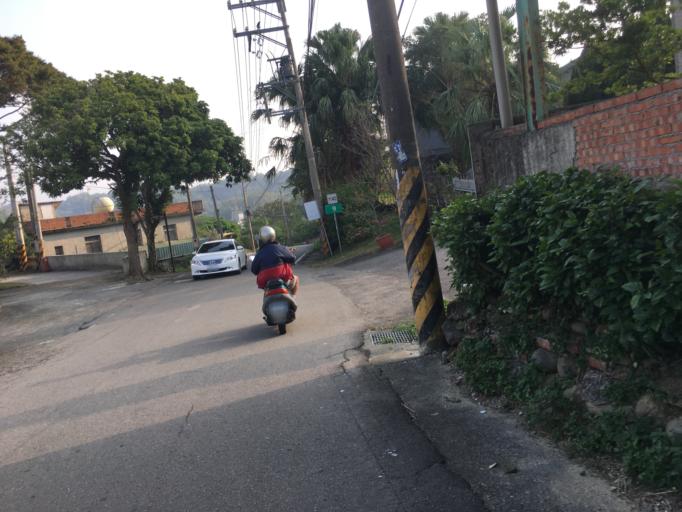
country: TW
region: Taiwan
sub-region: Hsinchu
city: Hsinchu
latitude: 24.7374
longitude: 121.0263
